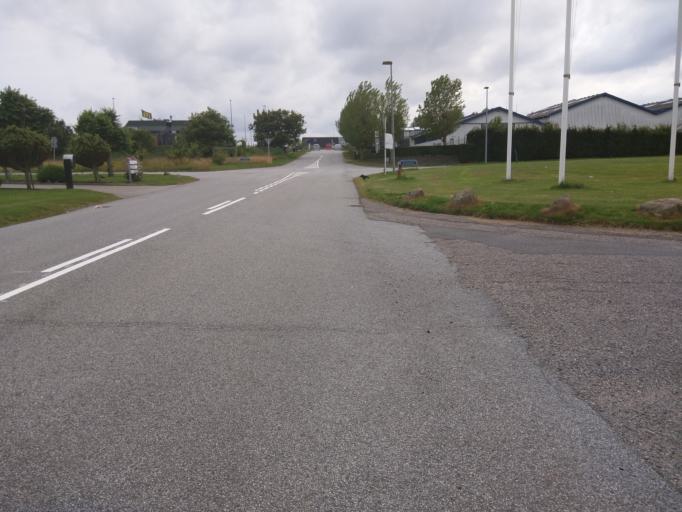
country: DK
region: Central Jutland
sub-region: Viborg Kommune
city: Viborg
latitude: 56.4492
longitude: 9.3649
